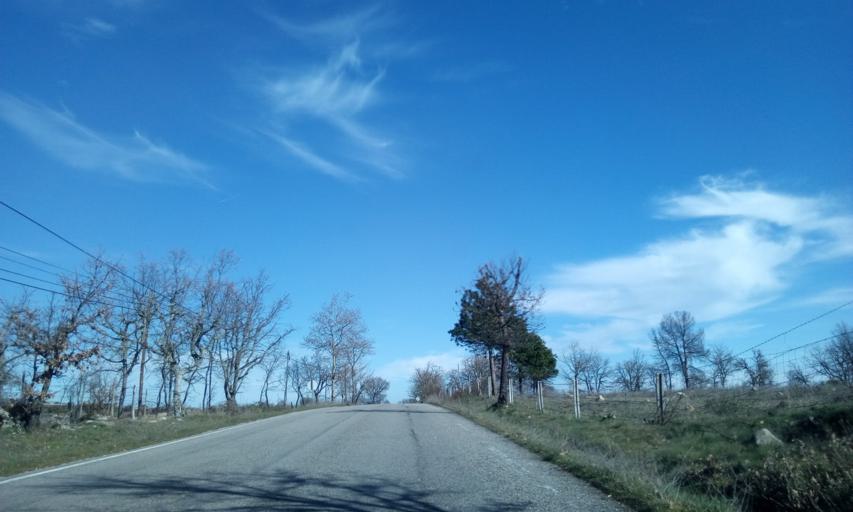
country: PT
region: Guarda
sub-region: Guarda
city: Sequeira
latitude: 40.6004
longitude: -7.0957
